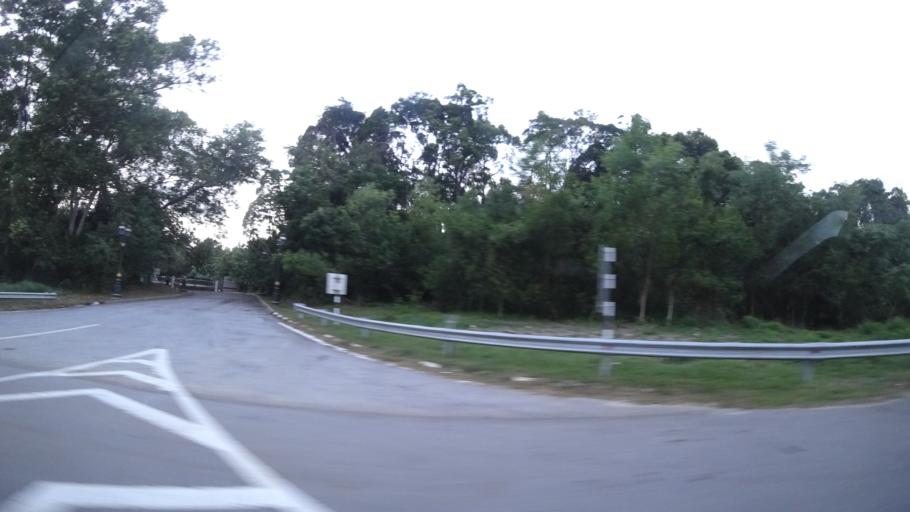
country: BN
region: Brunei and Muara
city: Bandar Seri Begawan
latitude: 4.9296
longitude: 114.8165
